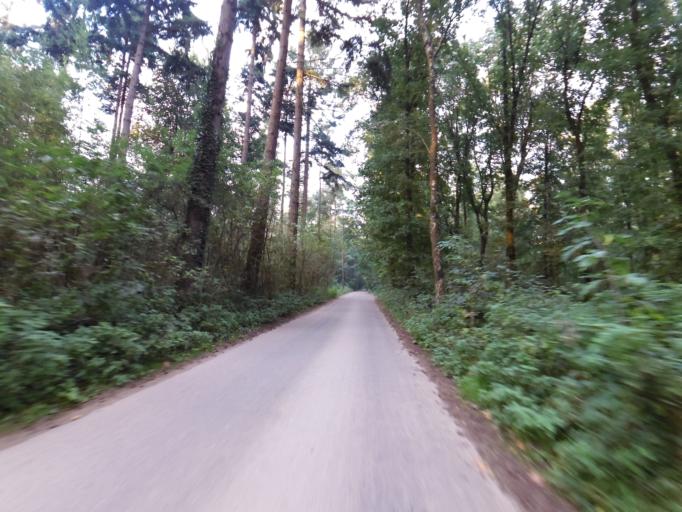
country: NL
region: Gelderland
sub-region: Gemeente Doesburg
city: Doesburg
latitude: 51.9456
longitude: 6.1922
